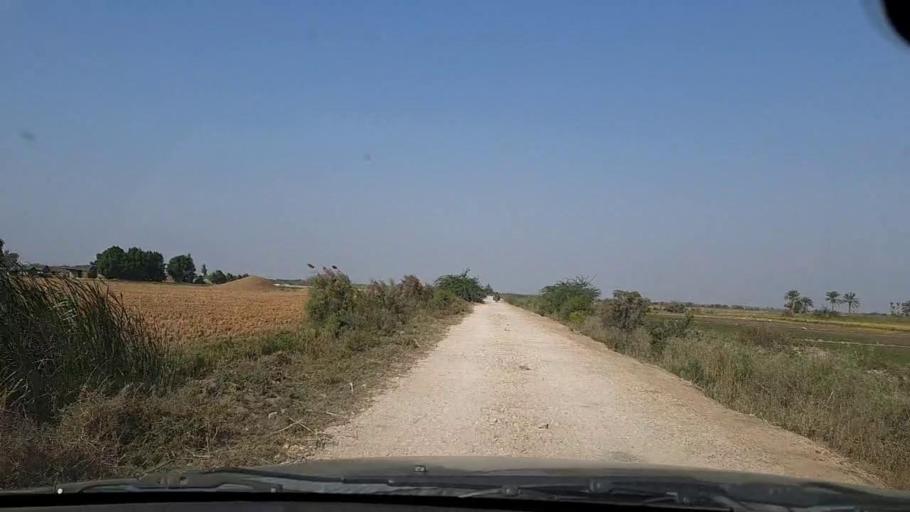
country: PK
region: Sindh
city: Mirpur Sakro
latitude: 24.3742
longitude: 67.6830
